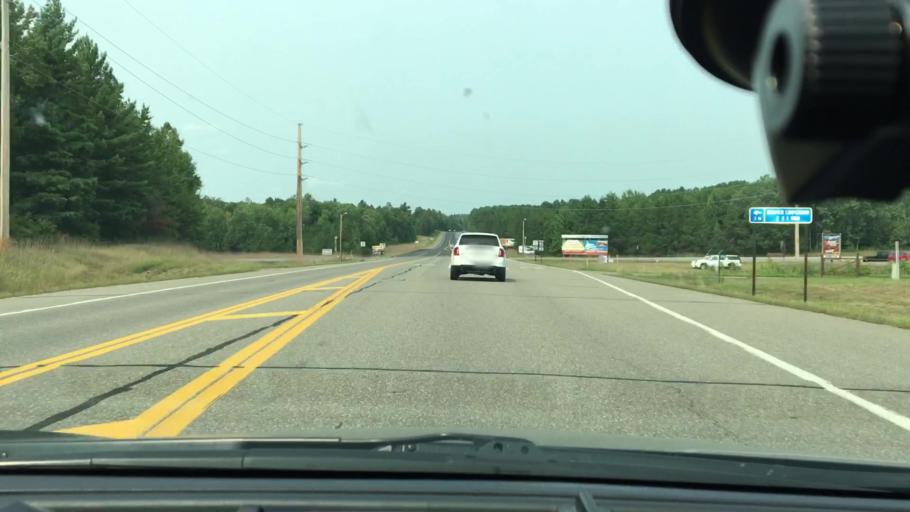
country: US
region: Minnesota
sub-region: Crow Wing County
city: Cross Lake
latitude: 46.6157
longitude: -94.1318
